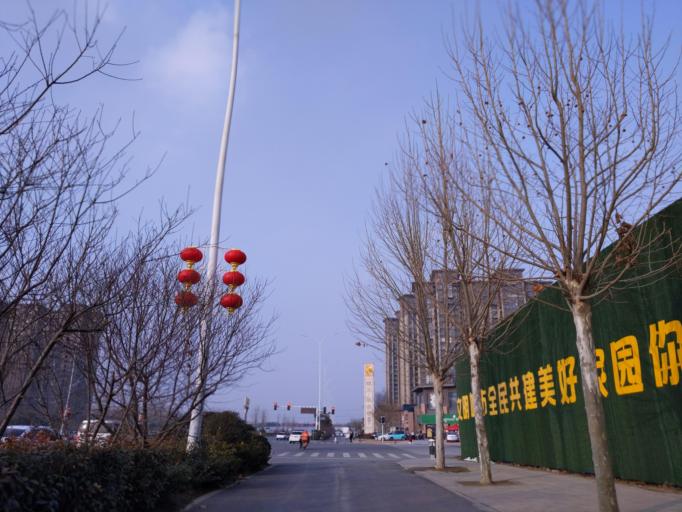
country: CN
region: Henan Sheng
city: Puyang
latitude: 35.8130
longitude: 115.0226
